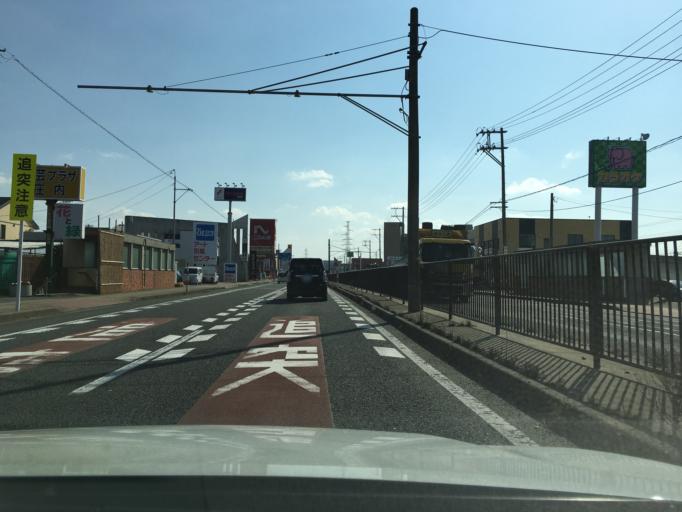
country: JP
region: Yamagata
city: Sakata
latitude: 38.9033
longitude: 139.8565
